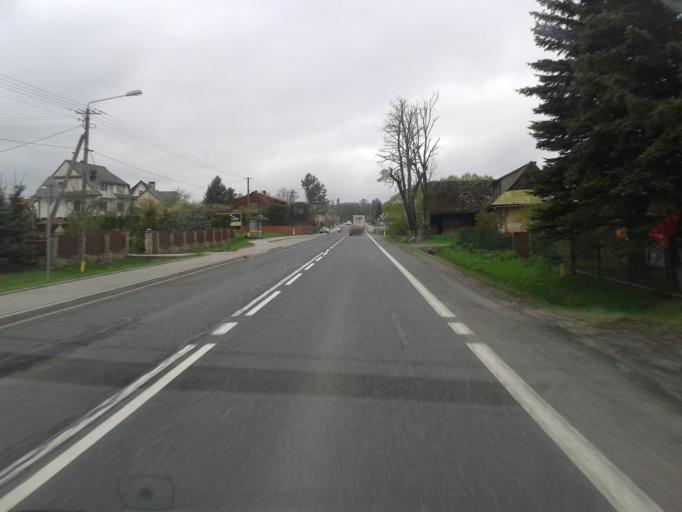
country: PL
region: Lesser Poland Voivodeship
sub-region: Powiat nowotarski
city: Spytkowice
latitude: 49.5765
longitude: 19.8373
